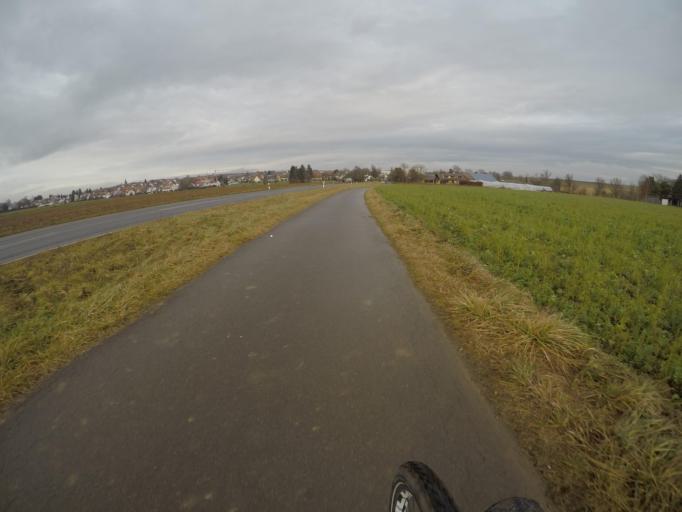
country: DE
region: Baden-Wuerttemberg
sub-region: Regierungsbezirk Stuttgart
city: Filderstadt
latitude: 48.6422
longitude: 9.2503
